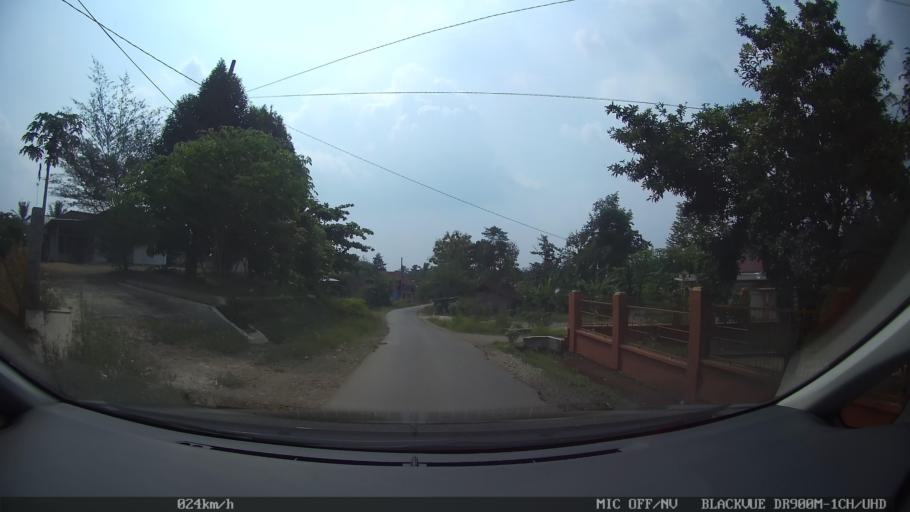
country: ID
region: Lampung
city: Gadingrejo
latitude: -5.3588
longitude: 105.0410
